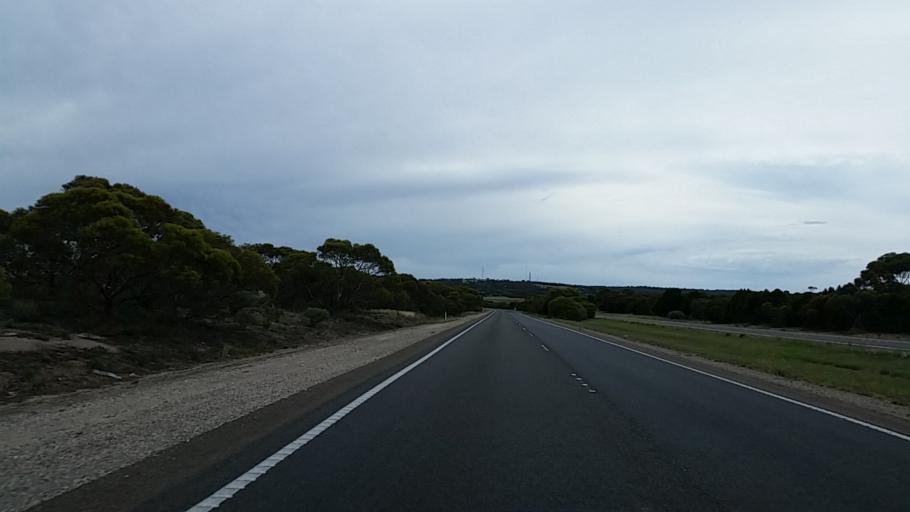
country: AU
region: South Australia
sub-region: Murray Bridge
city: Murray Bridge
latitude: -35.1458
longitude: 139.2543
